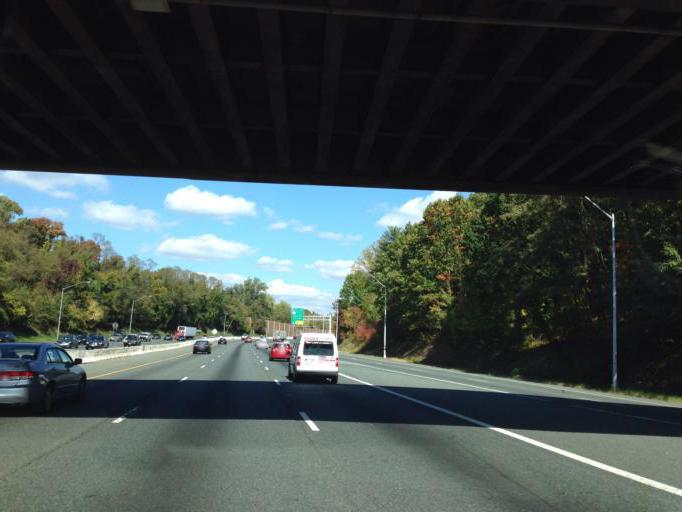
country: US
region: Maryland
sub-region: Baltimore County
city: Pikesville
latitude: 39.3768
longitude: -76.7444
